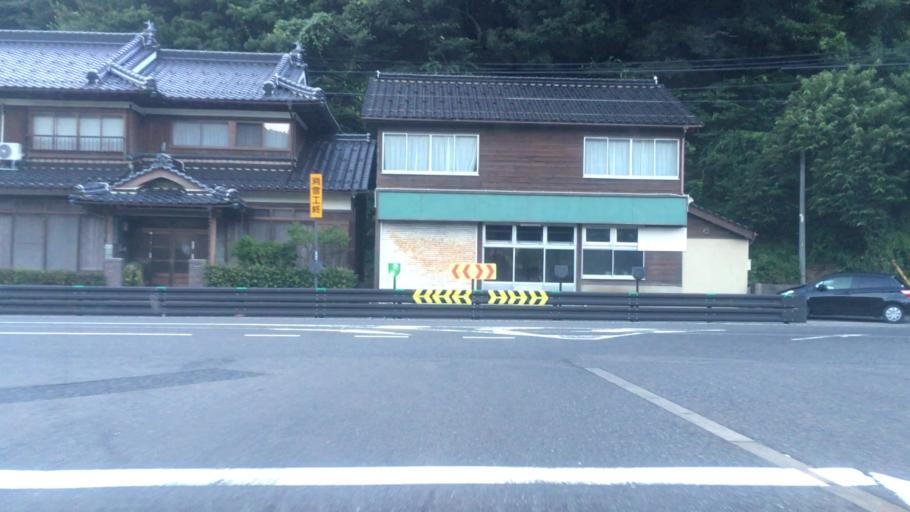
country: JP
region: Tottori
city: Tottori
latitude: 35.6148
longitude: 134.3929
